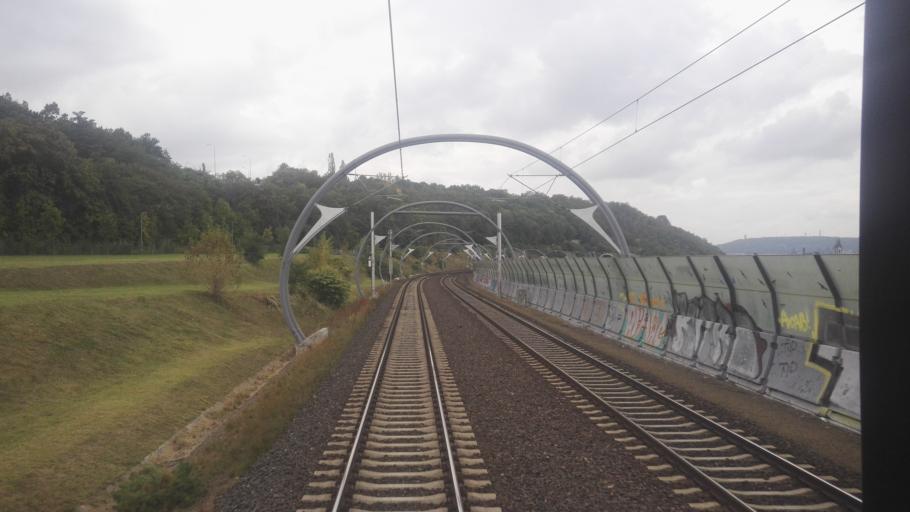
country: CZ
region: Praha
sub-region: Praha 8
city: Liben
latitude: 50.0941
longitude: 14.4709
